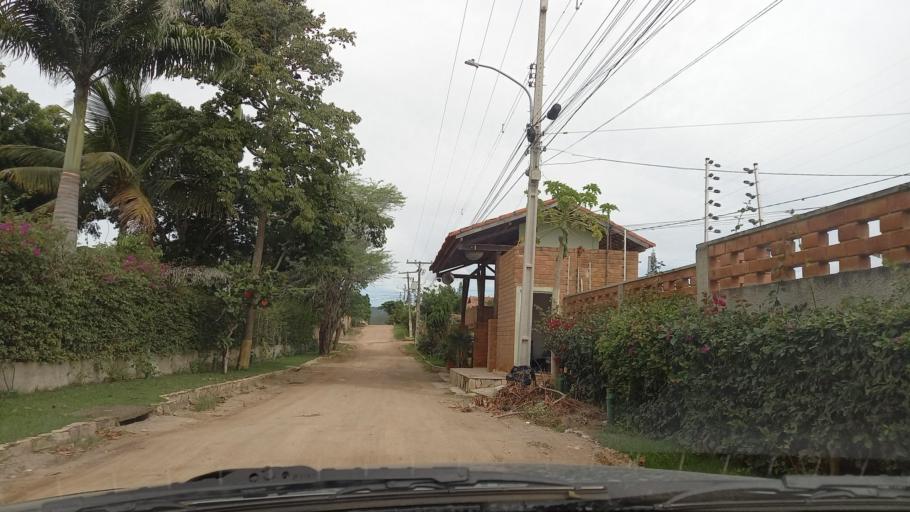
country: BR
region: Pernambuco
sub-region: Gravata
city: Gravata
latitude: -8.1947
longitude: -35.5942
